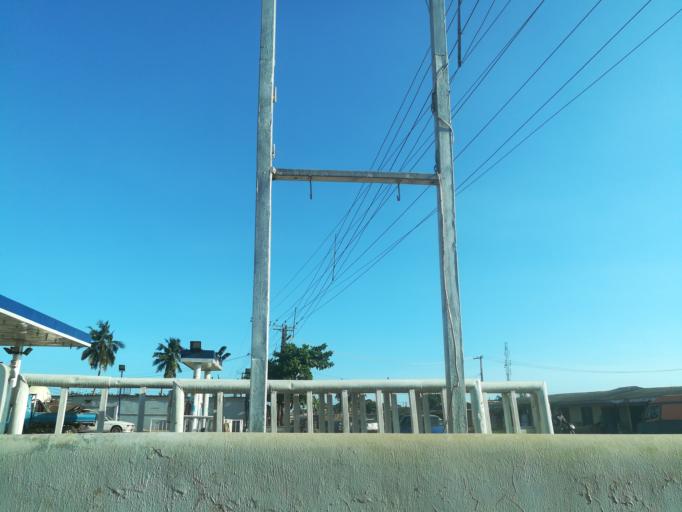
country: NG
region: Lagos
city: Ikorodu
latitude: 6.5812
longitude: 3.5254
